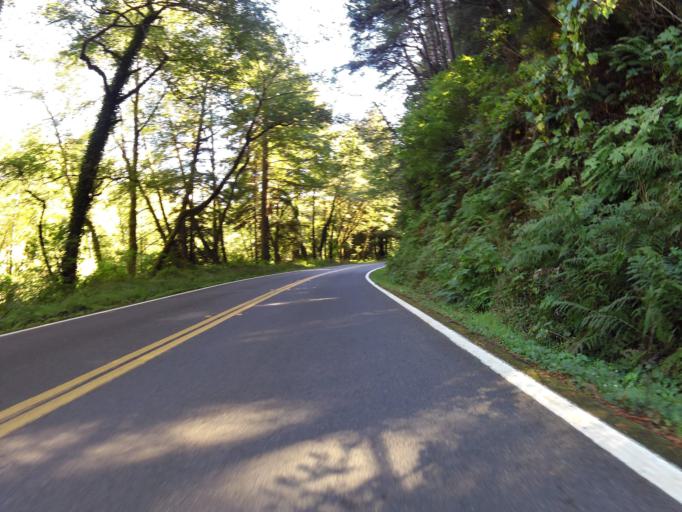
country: US
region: California
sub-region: Mendocino County
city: Fort Bragg
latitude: 39.7377
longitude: -123.8163
